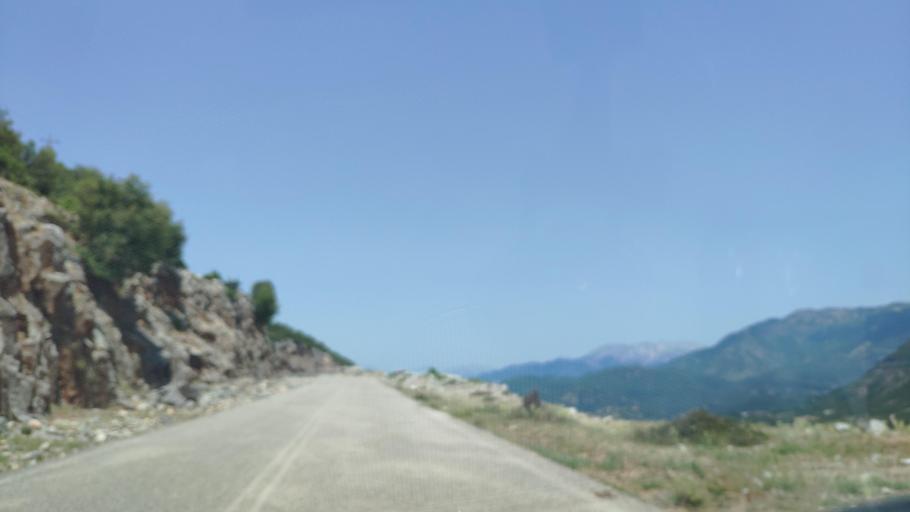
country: GR
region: Thessaly
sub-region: Nomos Kardhitsas
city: Anthiro
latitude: 39.1207
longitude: 21.4022
